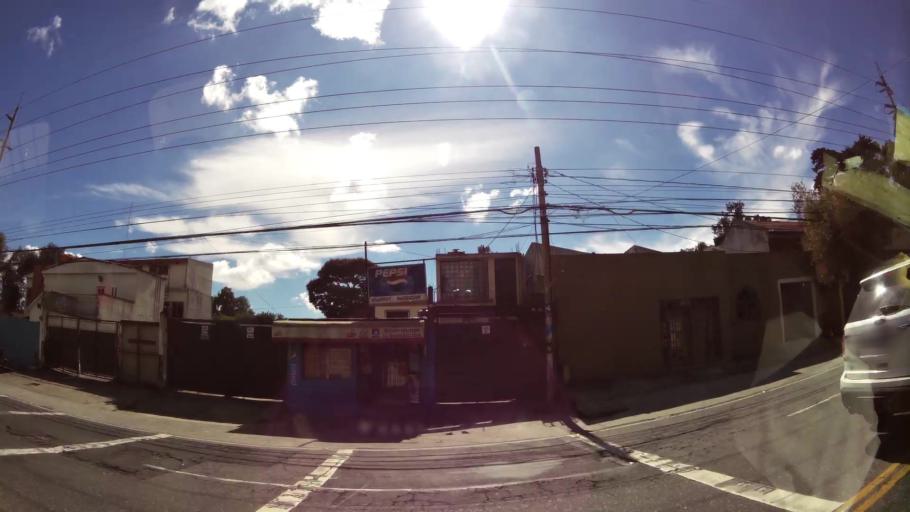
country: GT
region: Guatemala
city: Mixco
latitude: 14.6340
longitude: -90.5658
